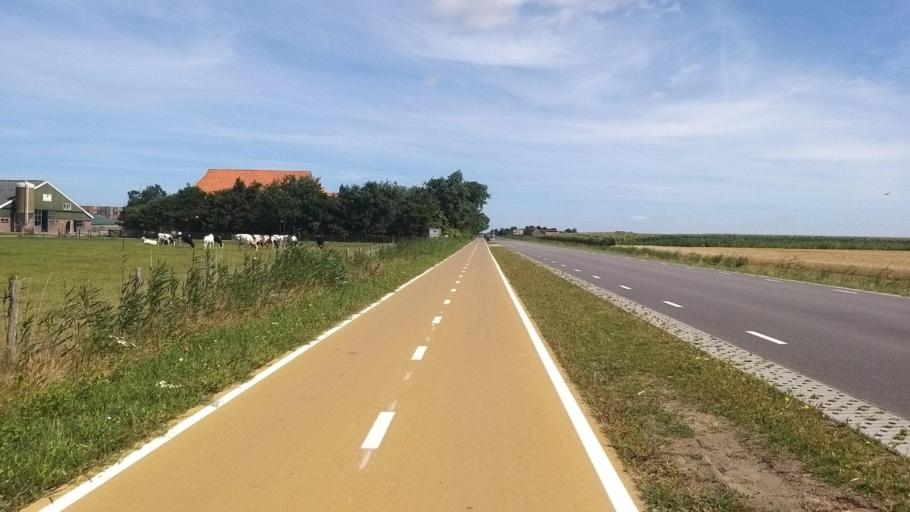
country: NL
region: North Holland
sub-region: Gemeente Texel
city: Den Burg
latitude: 53.1046
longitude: 4.8106
